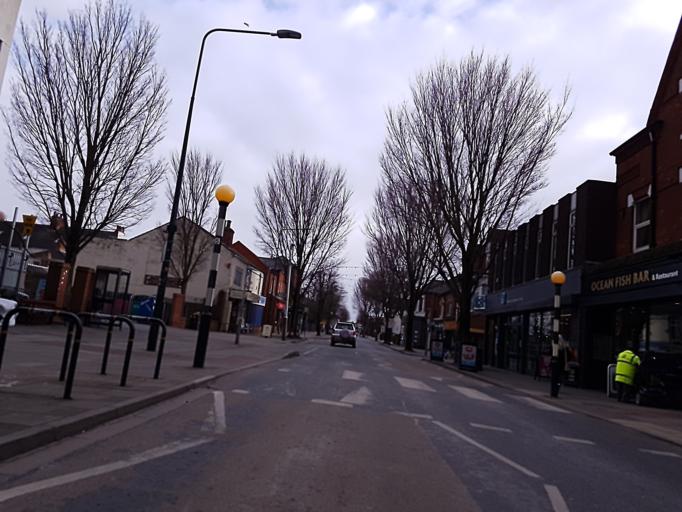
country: GB
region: England
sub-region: North East Lincolnshire
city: Cleethorpes
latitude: 53.5589
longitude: -0.0312
